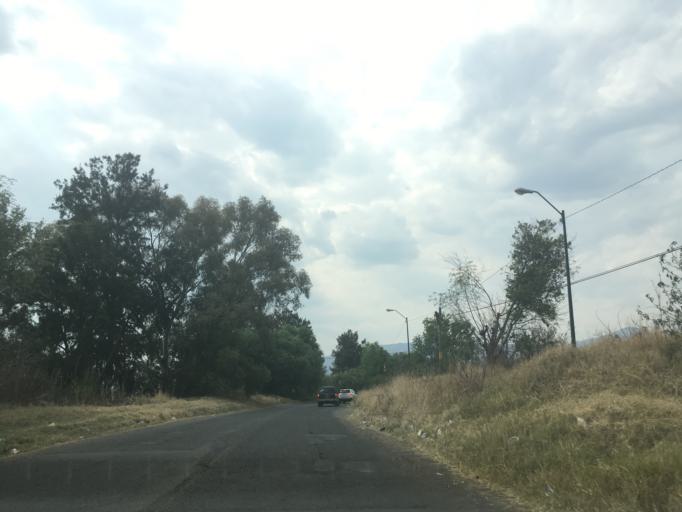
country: MX
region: Michoacan
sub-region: Morelia
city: Morelos
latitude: 19.6618
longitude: -101.2304
